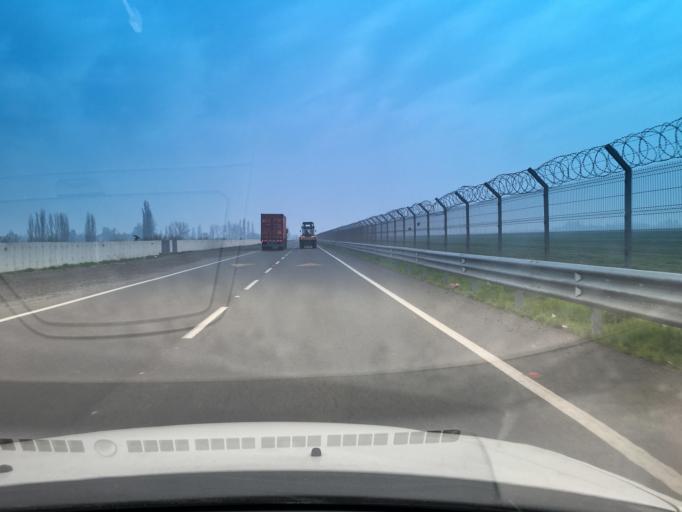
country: CL
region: Santiago Metropolitan
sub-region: Provincia de Santiago
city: Lo Prado
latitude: -33.3945
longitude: -70.8043
